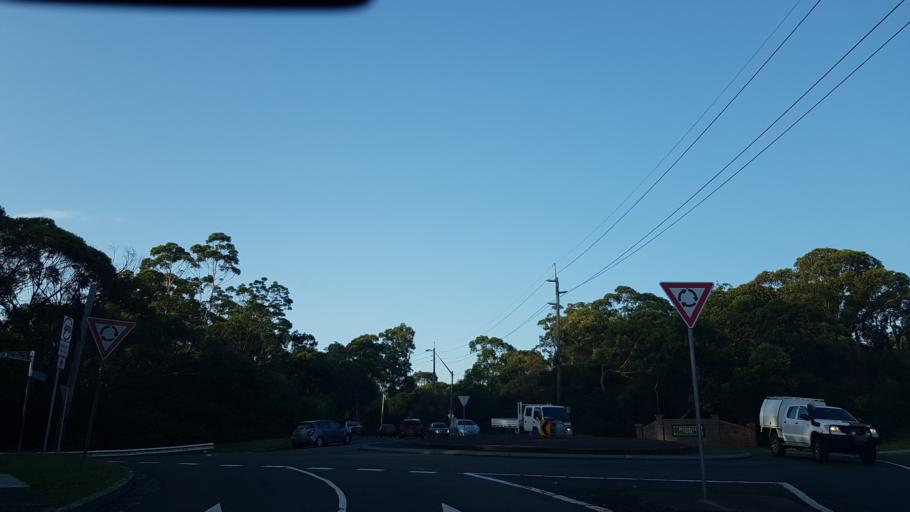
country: AU
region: New South Wales
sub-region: Warringah
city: Narraweena
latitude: -33.7474
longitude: 151.2628
